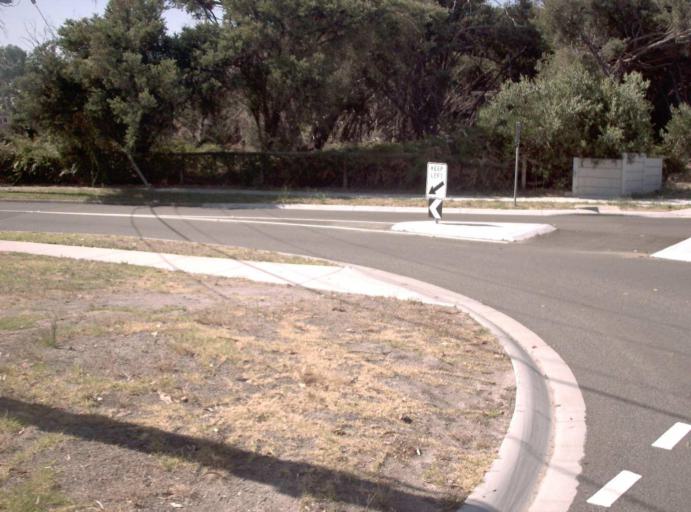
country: AU
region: Victoria
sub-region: Frankston
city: Frankston North
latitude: -38.1107
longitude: 145.1594
